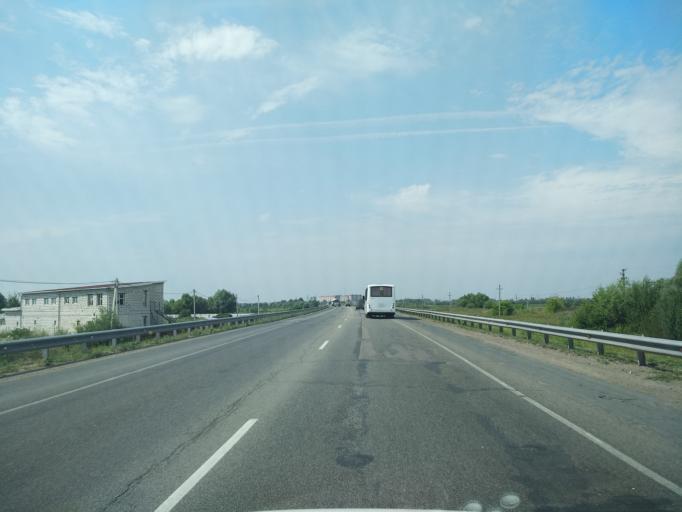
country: RU
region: Voronezj
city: Somovo
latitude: 51.6875
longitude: 39.3557
